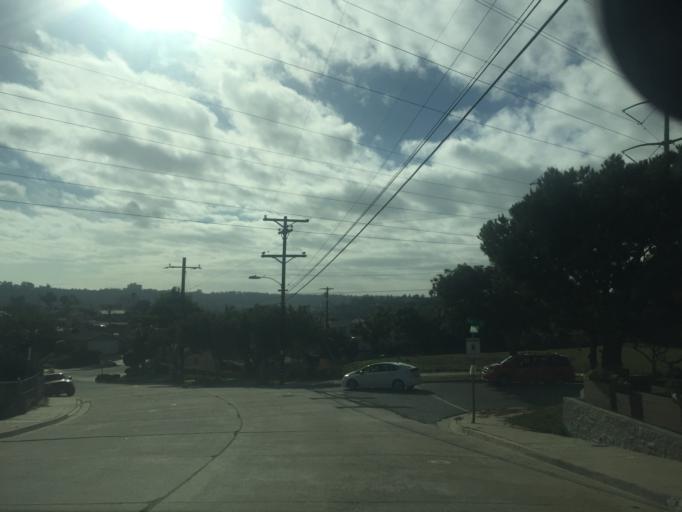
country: US
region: California
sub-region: San Diego County
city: San Diego
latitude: 32.7842
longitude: -117.1504
